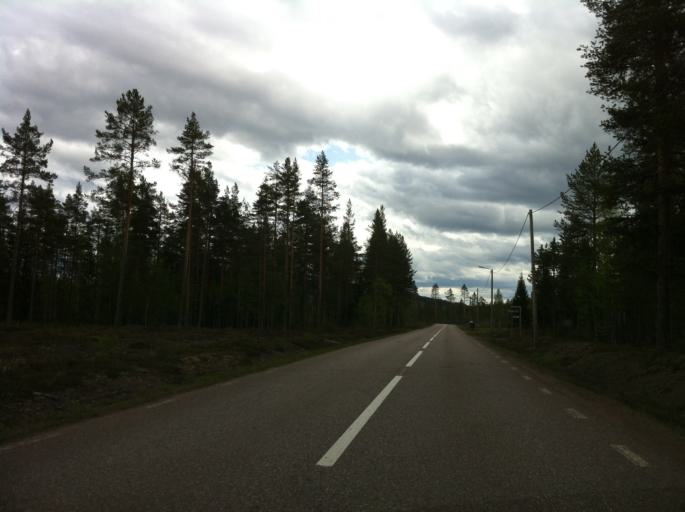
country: NO
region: Hedmark
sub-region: Trysil
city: Innbygda
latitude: 61.4293
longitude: 13.0904
